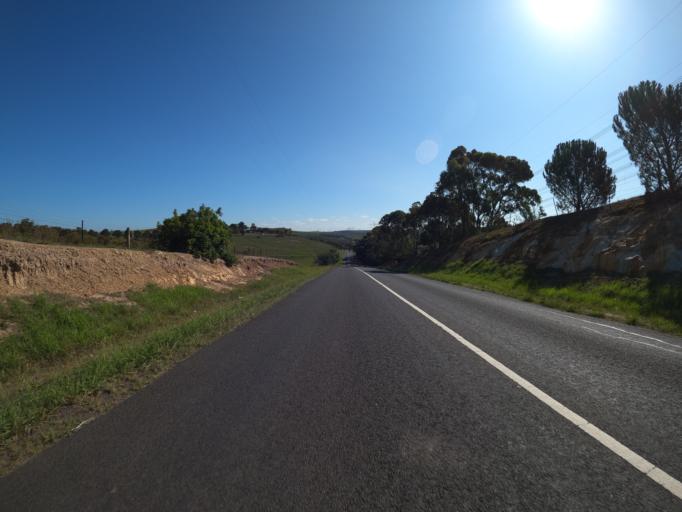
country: AU
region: Victoria
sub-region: Hume
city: Greenvale
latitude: -37.5517
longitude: 144.8578
